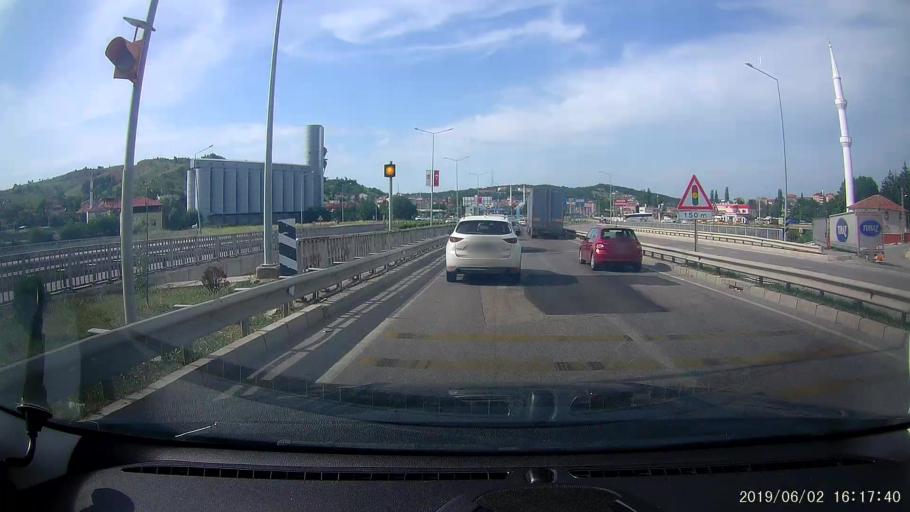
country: TR
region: Samsun
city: Havza
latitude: 40.9595
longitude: 35.6660
